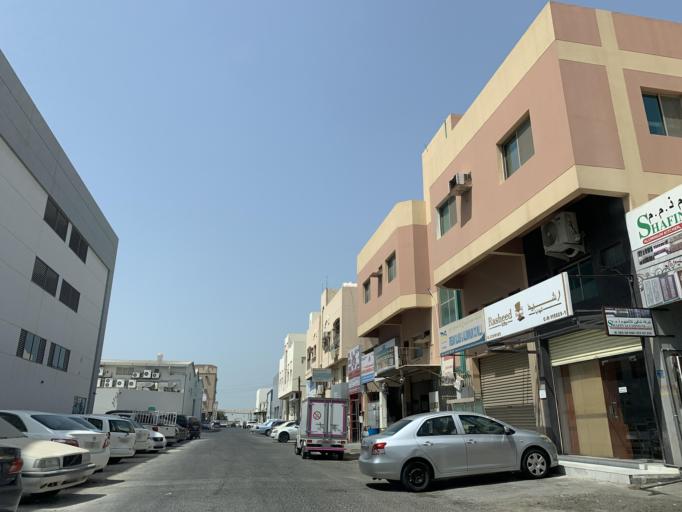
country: BH
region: Northern
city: Madinat `Isa
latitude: 26.1898
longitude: 50.5393
